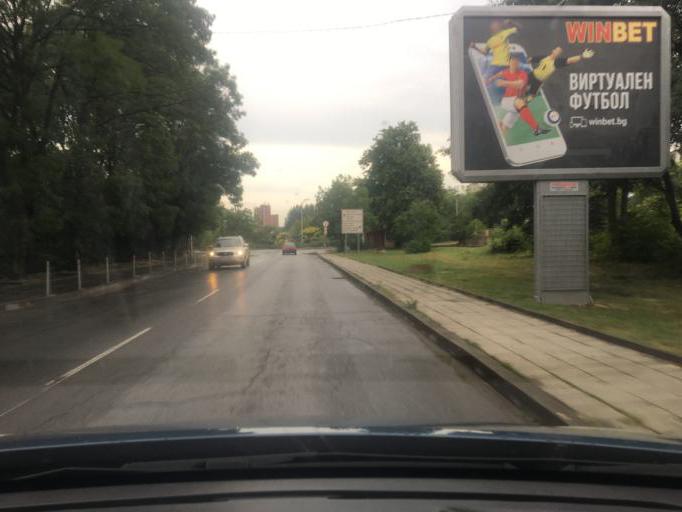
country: BG
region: Burgas
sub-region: Obshtina Burgas
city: Burgas
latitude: 42.5128
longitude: 27.4731
